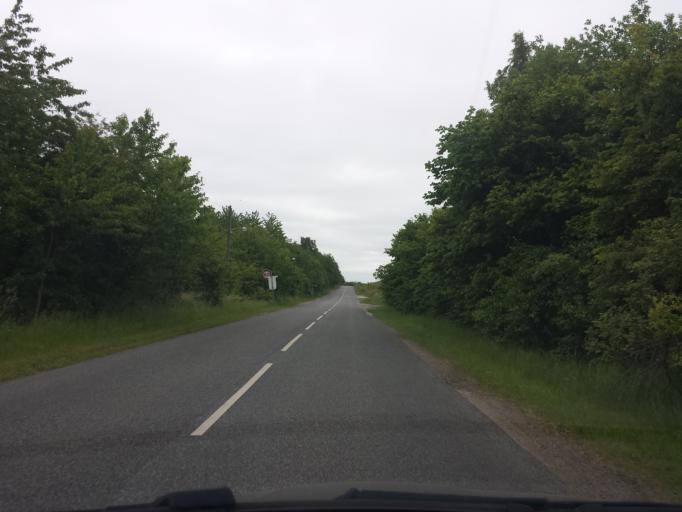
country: DK
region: Capital Region
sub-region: Ballerup Kommune
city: Ballerup
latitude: 55.6996
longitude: 12.3809
